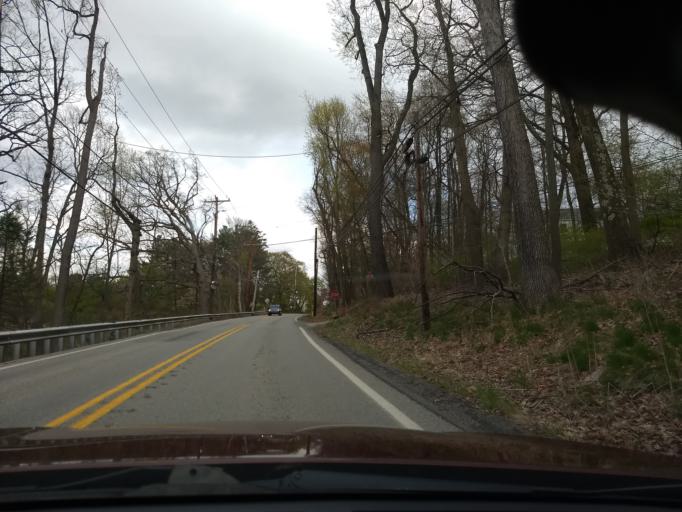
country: US
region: Pennsylvania
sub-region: Allegheny County
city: Fox Chapel
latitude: 40.5511
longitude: -79.8841
